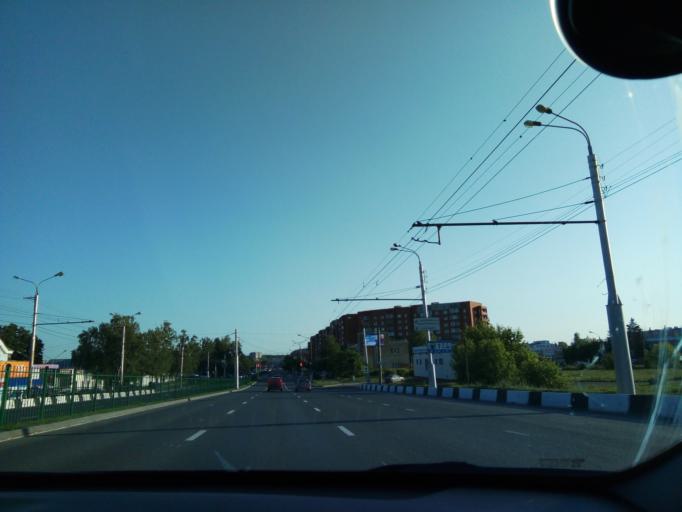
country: RU
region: Chuvashia
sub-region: Cheboksarskiy Rayon
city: Cheboksary
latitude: 56.1171
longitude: 47.2749
